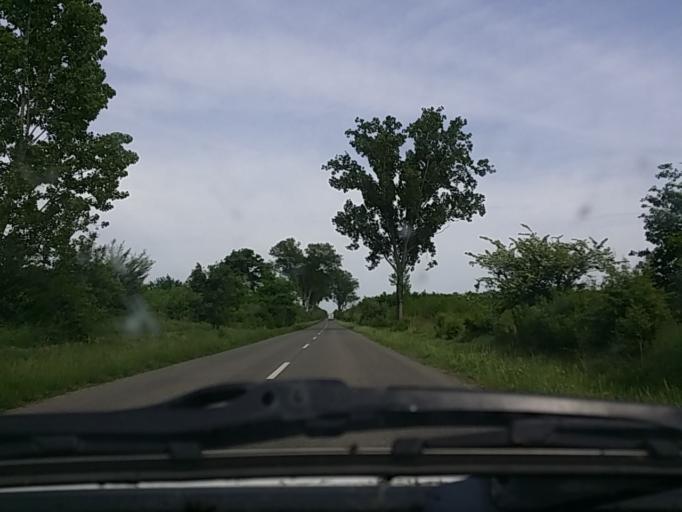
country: HU
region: Baranya
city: Sellye
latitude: 45.8812
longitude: 17.8848
